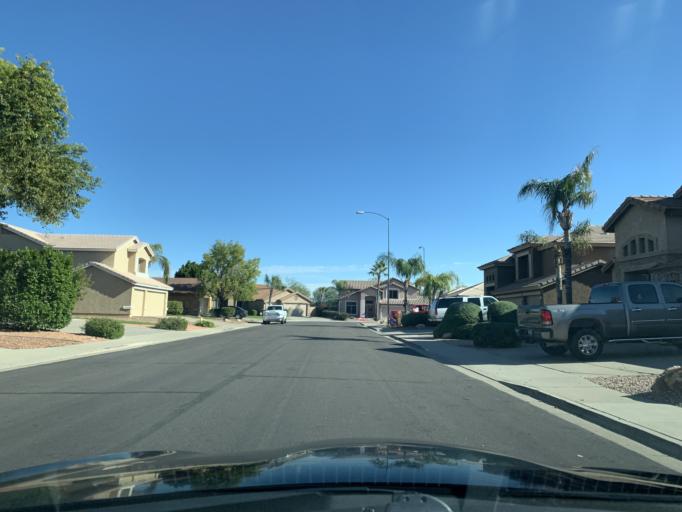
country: US
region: Arizona
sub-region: Pinal County
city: Apache Junction
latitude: 33.3834
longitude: -111.6211
